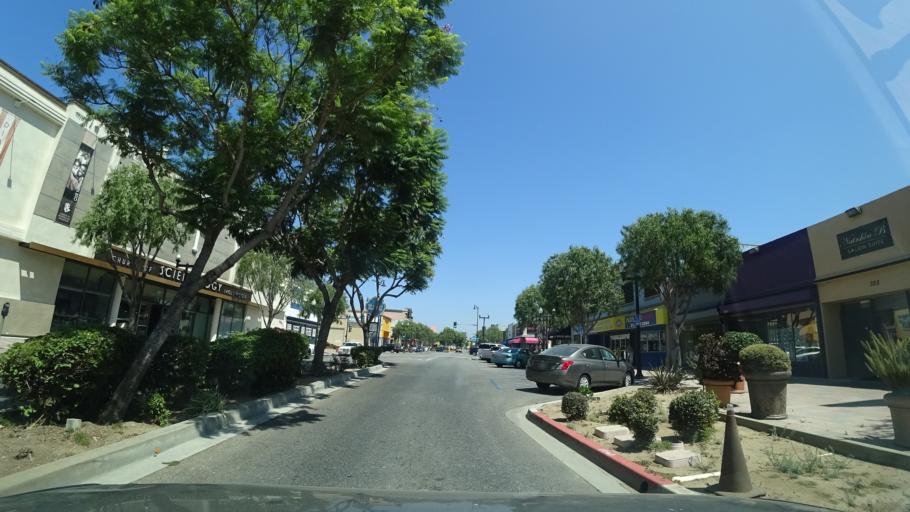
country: US
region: California
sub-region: Los Angeles County
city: Inglewood
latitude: 33.9601
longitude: -118.3519
